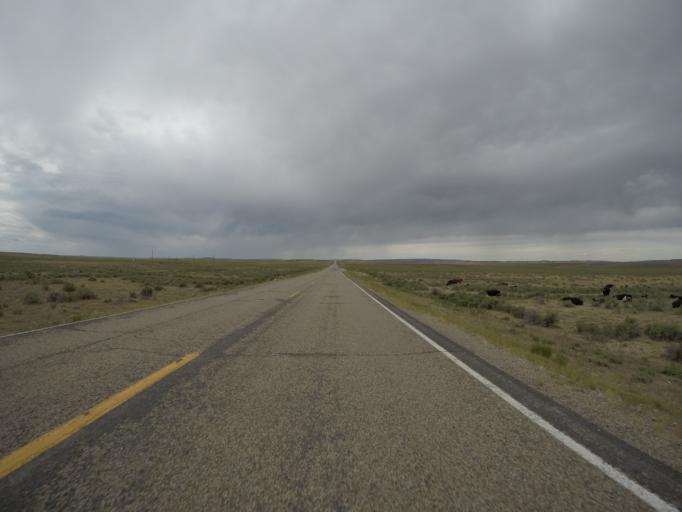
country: US
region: Wyoming
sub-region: Lincoln County
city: Kemmerer
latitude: 41.9635
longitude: -110.1390
